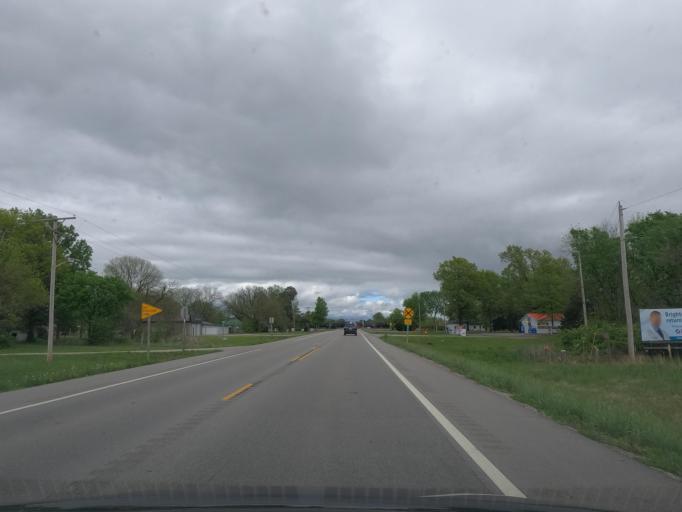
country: US
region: Kansas
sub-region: Crawford County
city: Pittsburg
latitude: 37.3394
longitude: -94.8238
